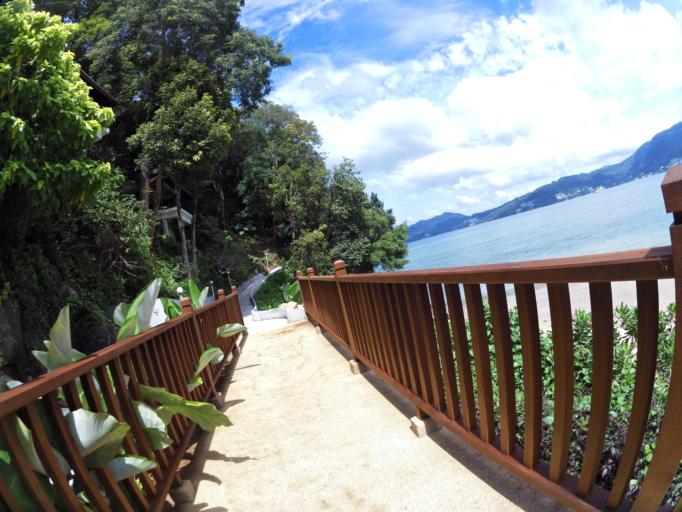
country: TH
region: Phuket
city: Patong
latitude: 7.8868
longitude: 98.2828
